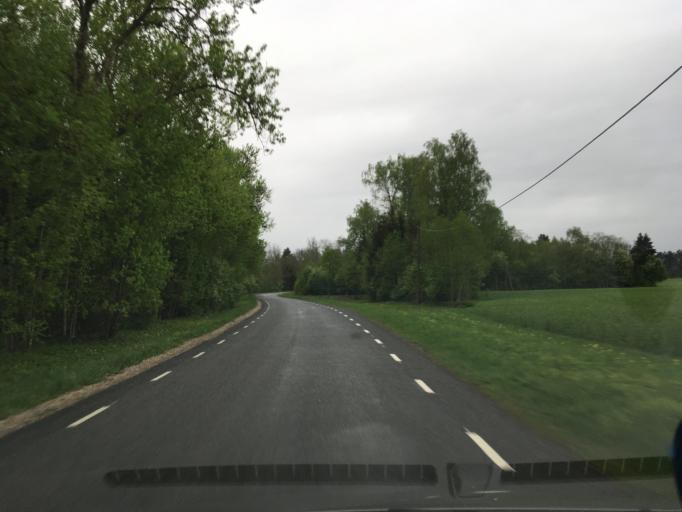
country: EE
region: Harju
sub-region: Keila linn
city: Keila
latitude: 59.2353
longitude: 24.4838
